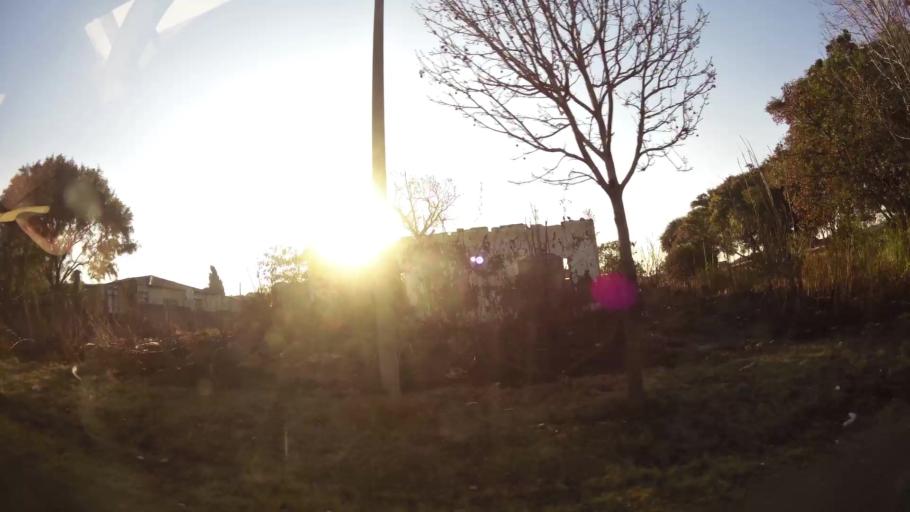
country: ZA
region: Gauteng
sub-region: West Rand District Municipality
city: Randfontein
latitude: -26.2246
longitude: 27.6475
